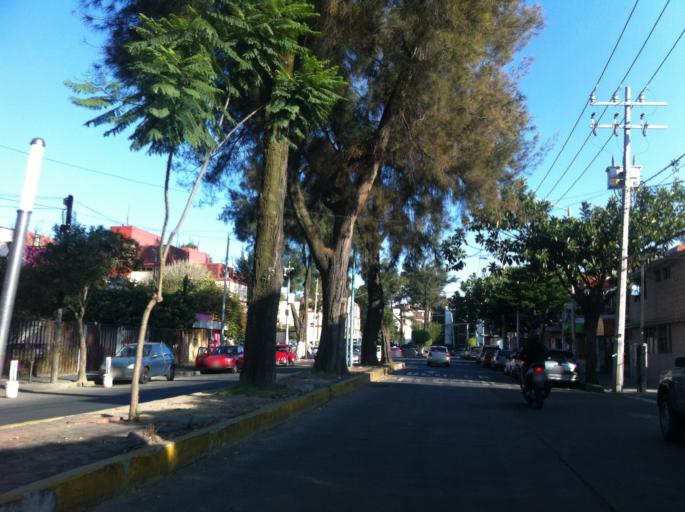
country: MX
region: Mexico City
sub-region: Iztacalco
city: Iztacalco
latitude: 19.4109
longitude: -99.1000
